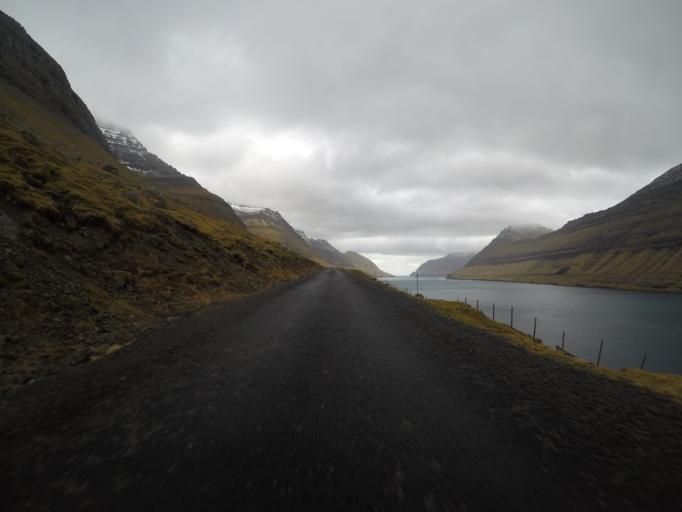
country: FO
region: Nordoyar
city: Klaksvik
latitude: 62.3071
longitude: -6.5409
